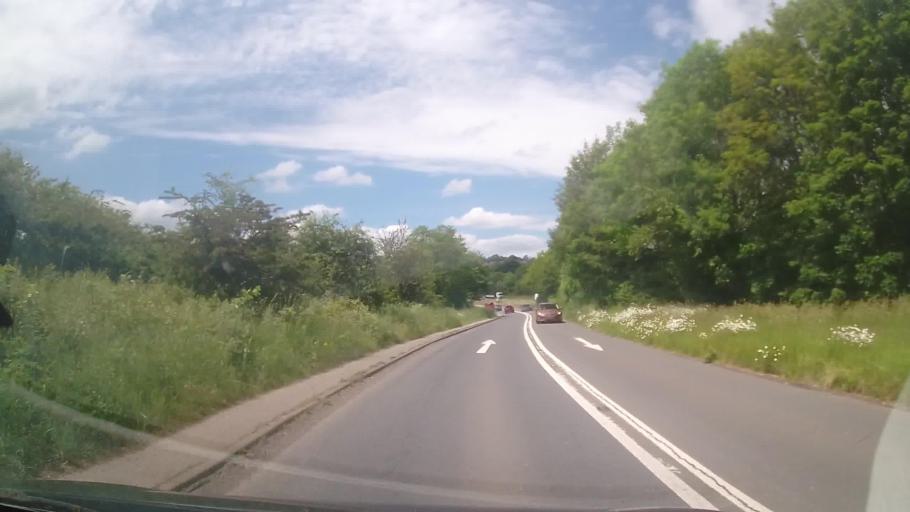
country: GB
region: England
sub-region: Devon
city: Ivybridge
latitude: 50.3856
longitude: -3.9321
